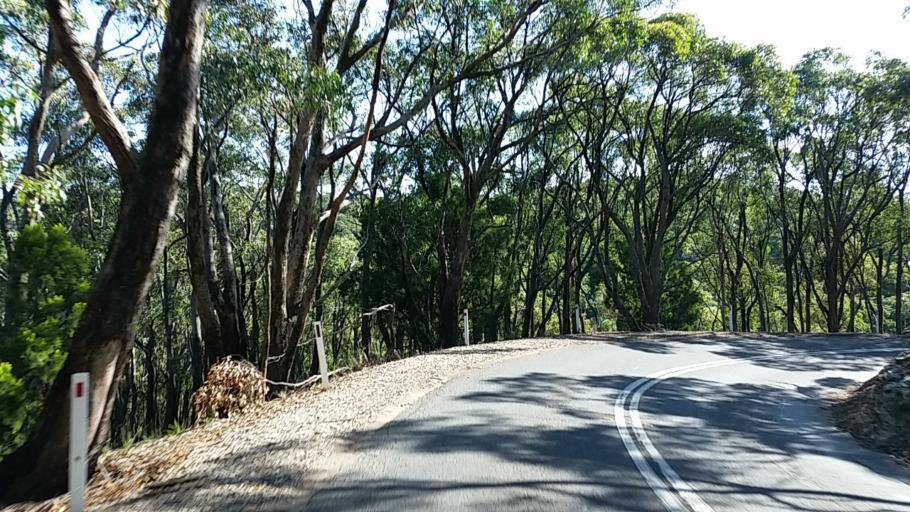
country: AU
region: South Australia
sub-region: Adelaide Hills
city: Crafers
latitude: -34.9649
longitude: 138.7128
